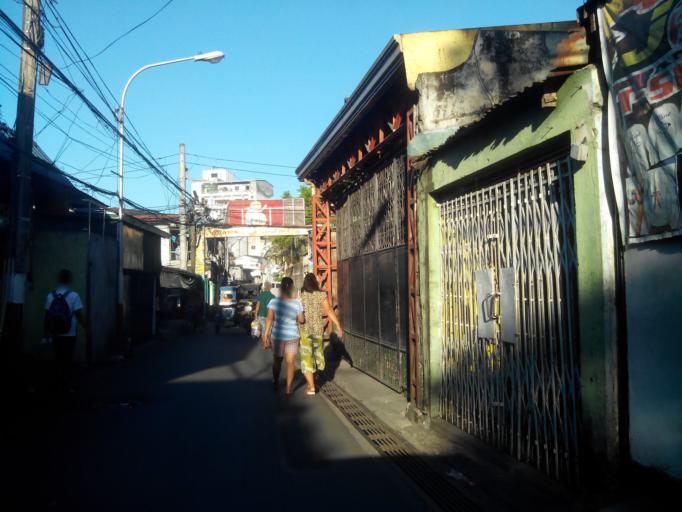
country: PH
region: Calabarzon
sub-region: Province of Rizal
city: Taytay
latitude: 14.5695
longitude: 121.1336
